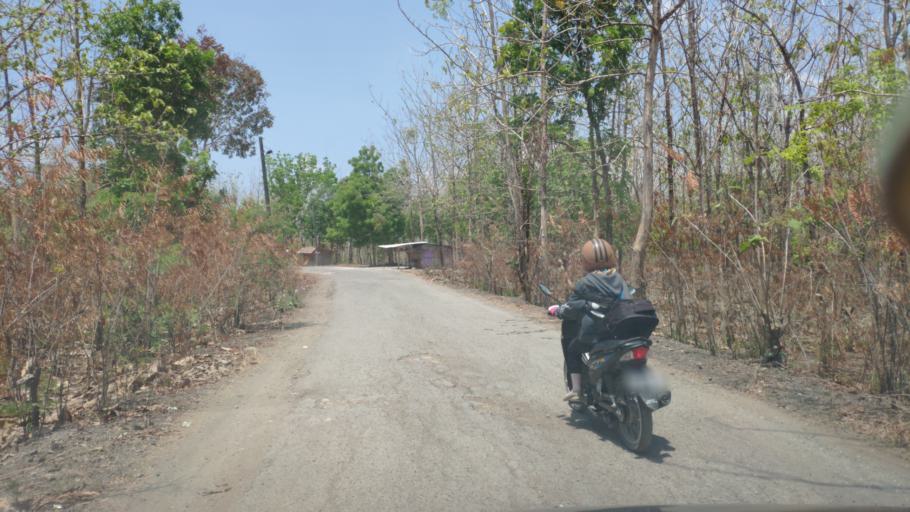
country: ID
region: Central Java
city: Randublatung
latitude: -7.2444
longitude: 111.3794
